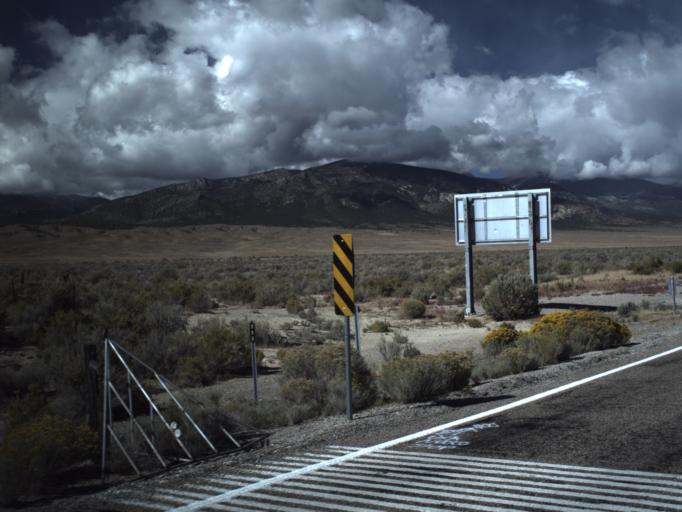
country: US
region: Nevada
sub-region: White Pine County
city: McGill
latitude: 38.9494
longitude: -114.0489
